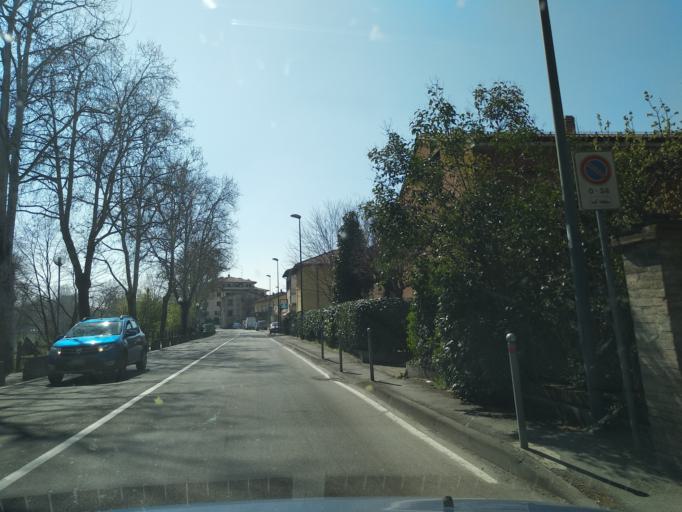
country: IT
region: Emilia-Romagna
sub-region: Provincia di Reggio Emilia
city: Reggio nell'Emilia
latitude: 44.7024
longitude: 10.6181
